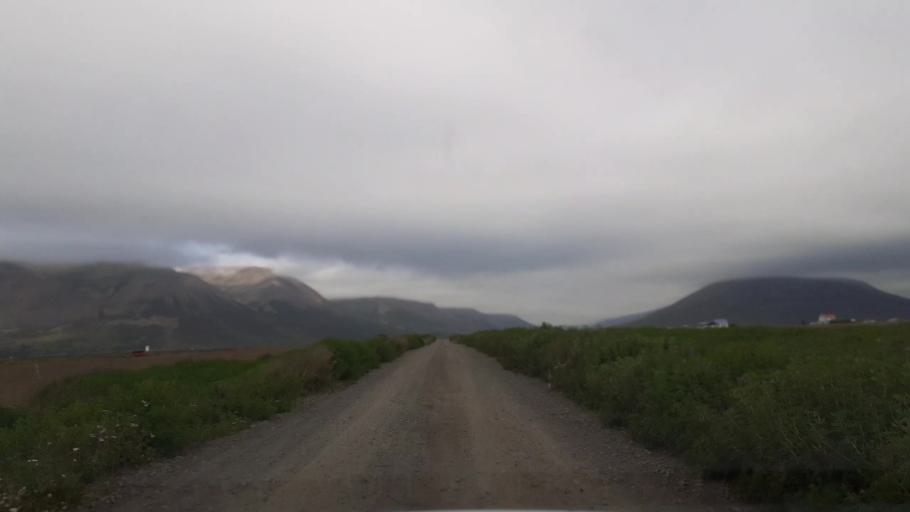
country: IS
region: Northwest
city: Saudarkrokur
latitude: 65.9028
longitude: -19.4205
